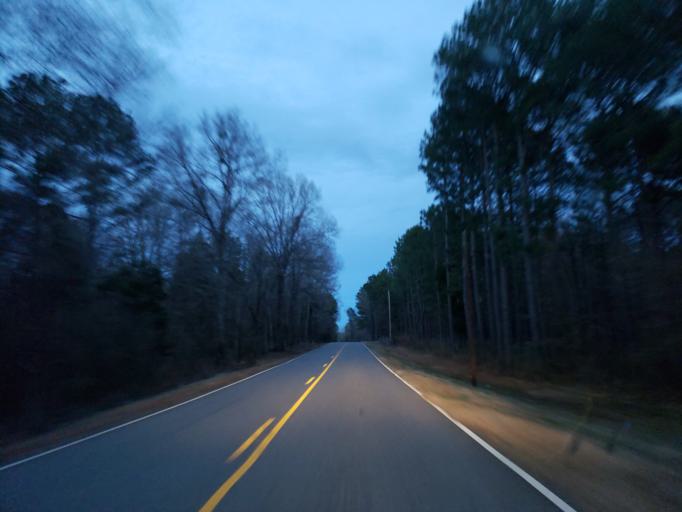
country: US
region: Alabama
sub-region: Greene County
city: Eutaw
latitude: 32.8842
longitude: -88.0587
